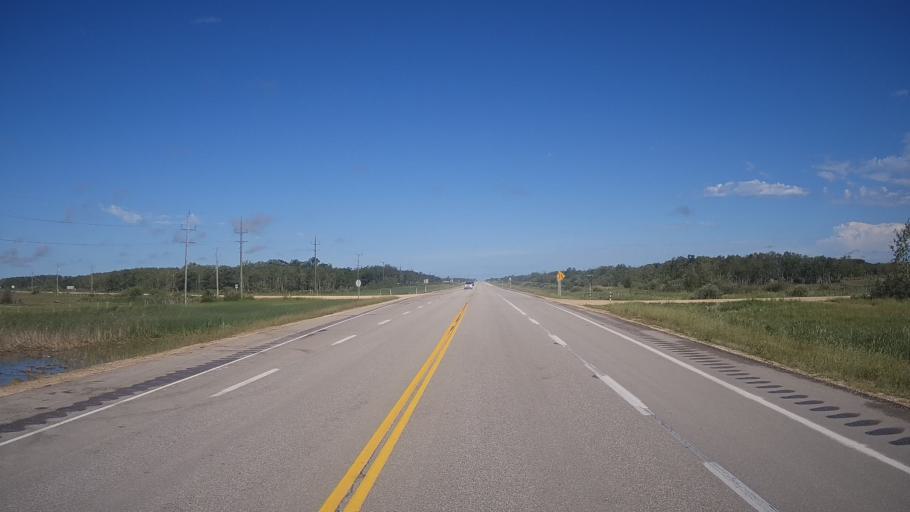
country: CA
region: Manitoba
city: Stonewall
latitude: 50.2403
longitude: -97.7135
